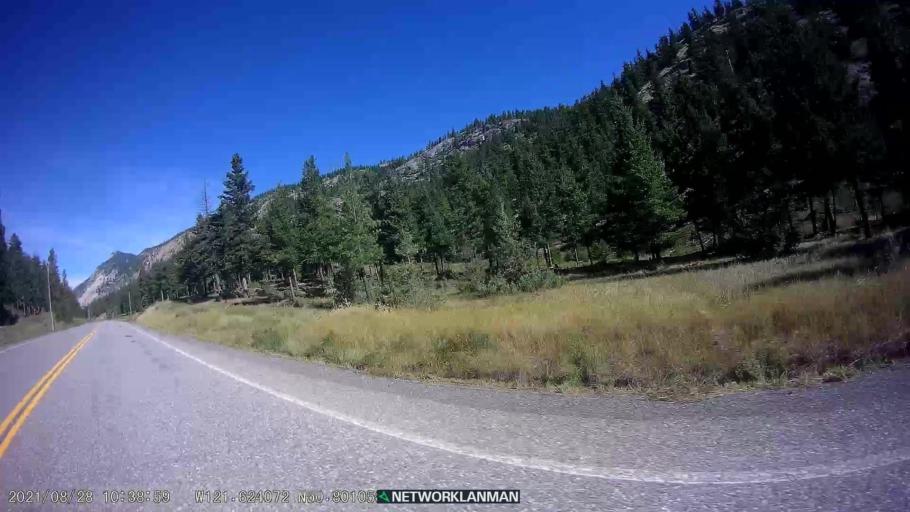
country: CA
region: British Columbia
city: Cache Creek
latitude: 50.8013
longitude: -121.6251
